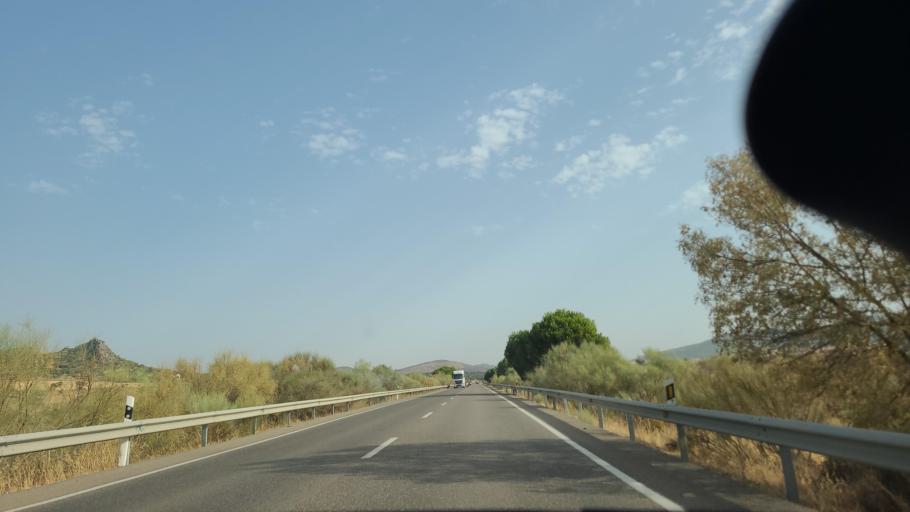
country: ES
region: Andalusia
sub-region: Province of Cordoba
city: Belmez
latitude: 38.2374
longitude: -5.1679
